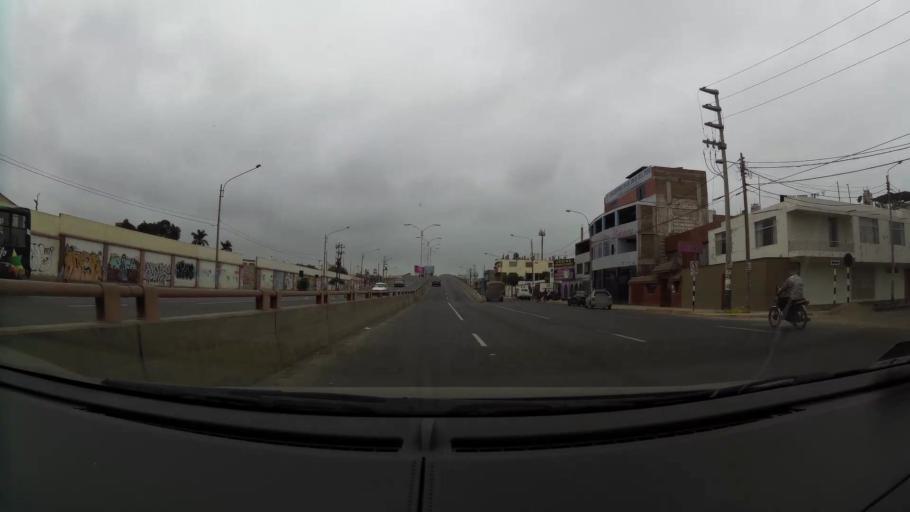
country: PE
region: La Libertad
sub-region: Provincia de Trujillo
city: Trujillo
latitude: -8.1252
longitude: -79.0255
